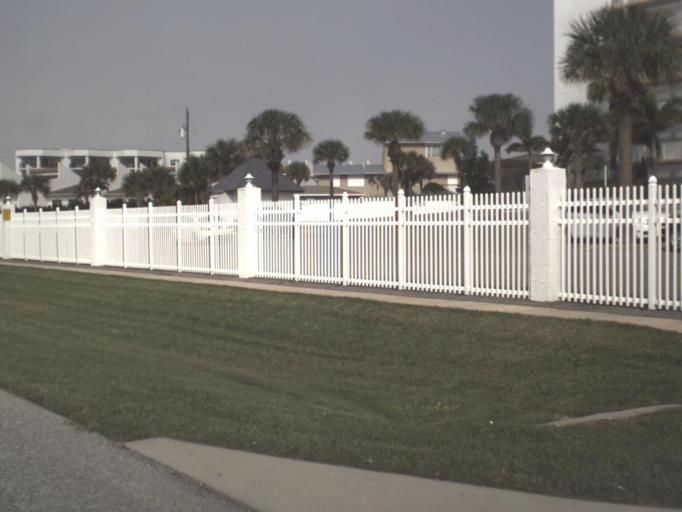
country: US
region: Florida
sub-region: Volusia County
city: Edgewater
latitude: 28.9760
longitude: -80.8577
